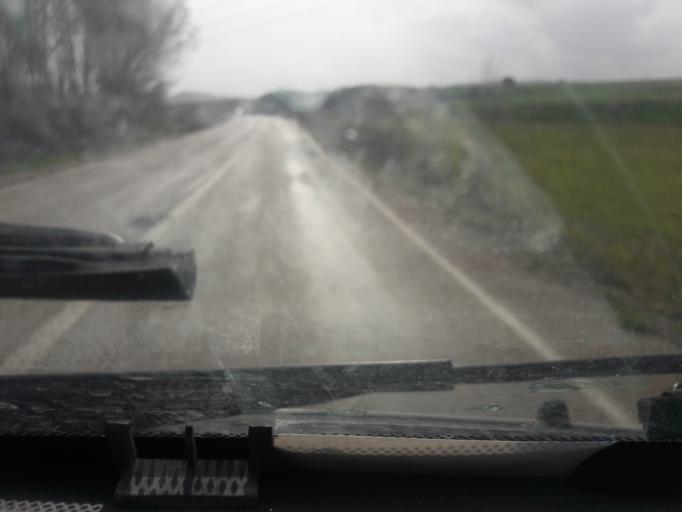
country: TR
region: Gumushane
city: Kelkit
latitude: 40.1301
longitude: 39.3614
